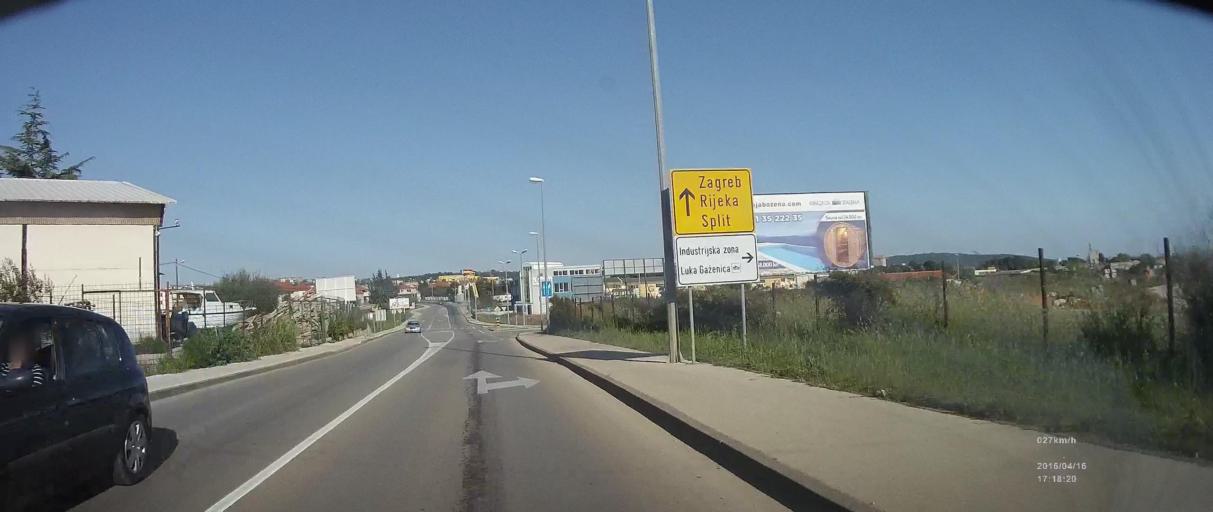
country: HR
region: Zadarska
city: Zadar
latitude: 44.1016
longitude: 15.2546
